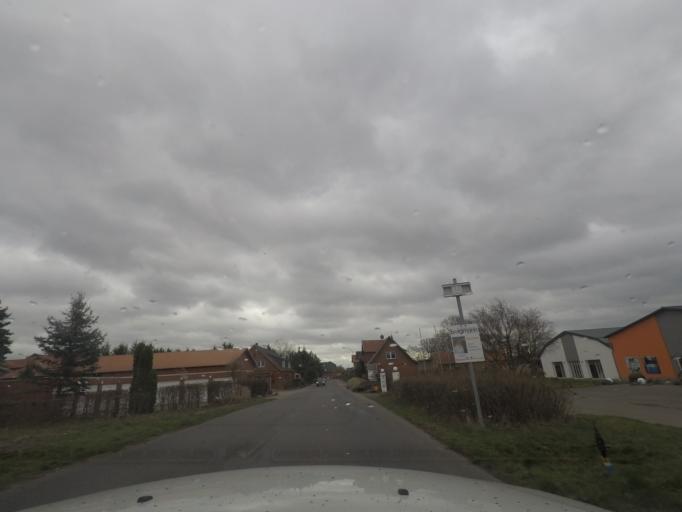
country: DE
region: Lower Saxony
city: Emmendorf
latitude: 53.0072
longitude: 10.6033
